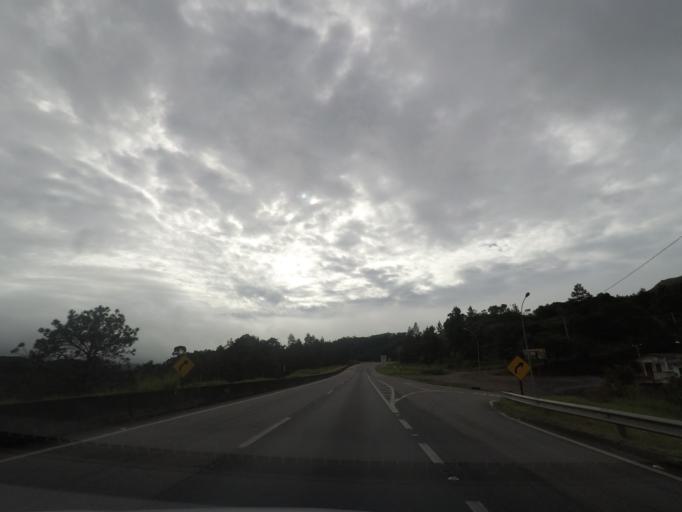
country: BR
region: Parana
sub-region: Campina Grande Do Sul
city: Campina Grande do Sul
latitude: -25.1085
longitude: -48.8362
